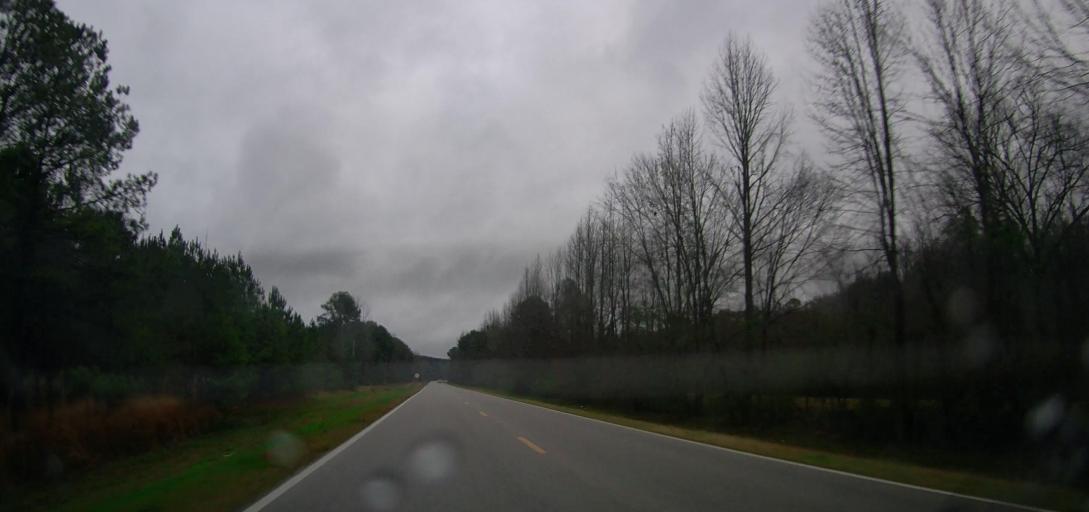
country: US
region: Alabama
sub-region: Bibb County
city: Centreville
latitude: 32.9239
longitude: -87.0405
